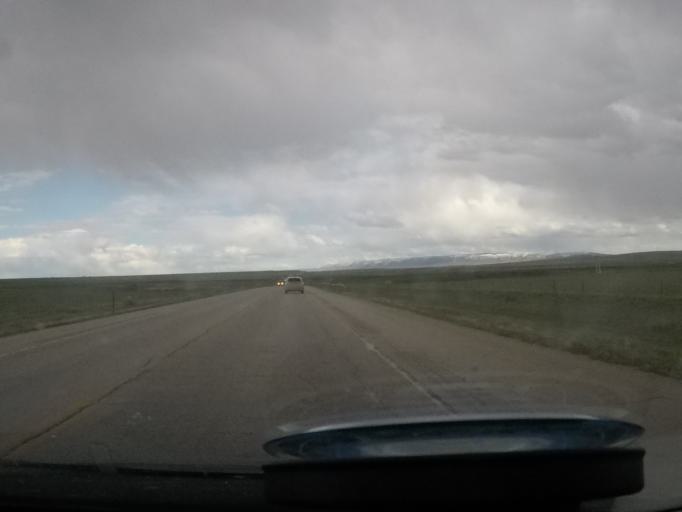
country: US
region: Wyoming
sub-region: Natrona County
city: Mills
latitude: 42.9541
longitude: -106.6433
